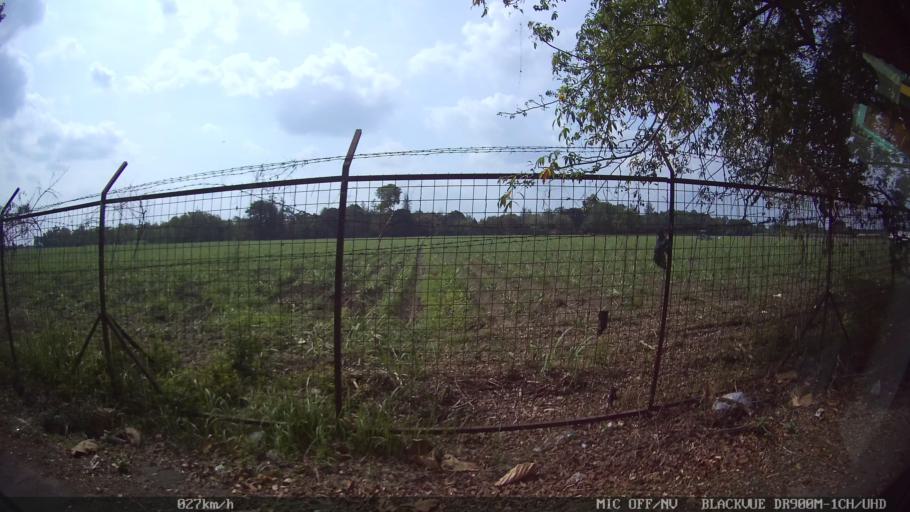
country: ID
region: Daerah Istimewa Yogyakarta
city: Depok
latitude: -7.8034
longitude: 110.4291
